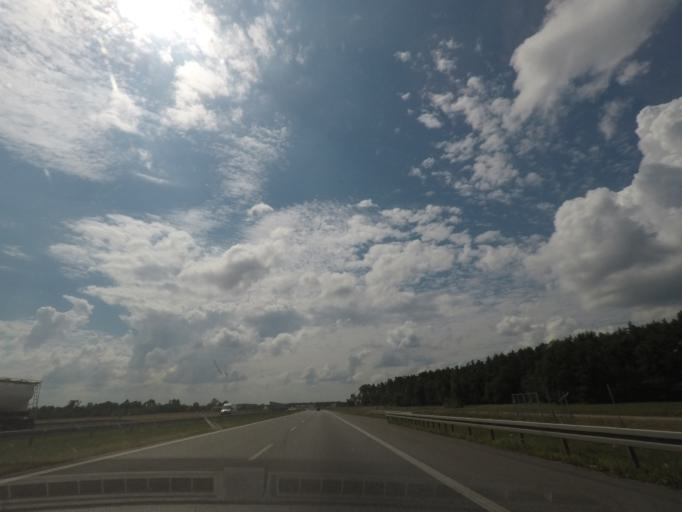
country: PL
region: Lodz Voivodeship
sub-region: Powiat leczycki
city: Piatek
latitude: 52.0229
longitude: 19.5420
